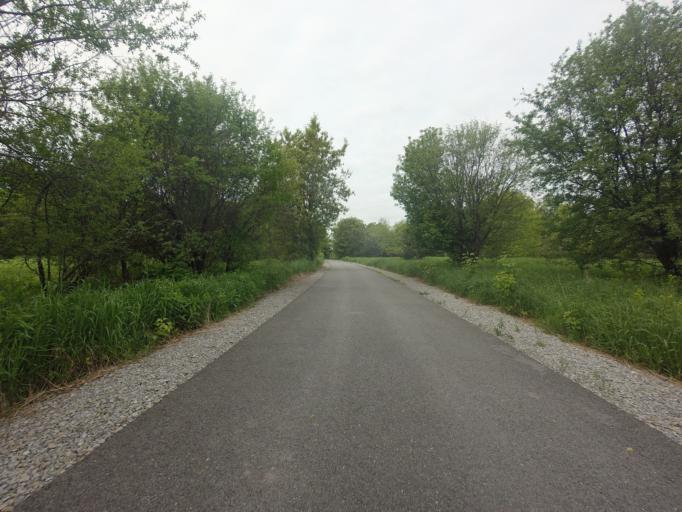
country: US
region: New York
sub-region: Jefferson County
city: Black River
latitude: 43.9985
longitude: -75.8134
